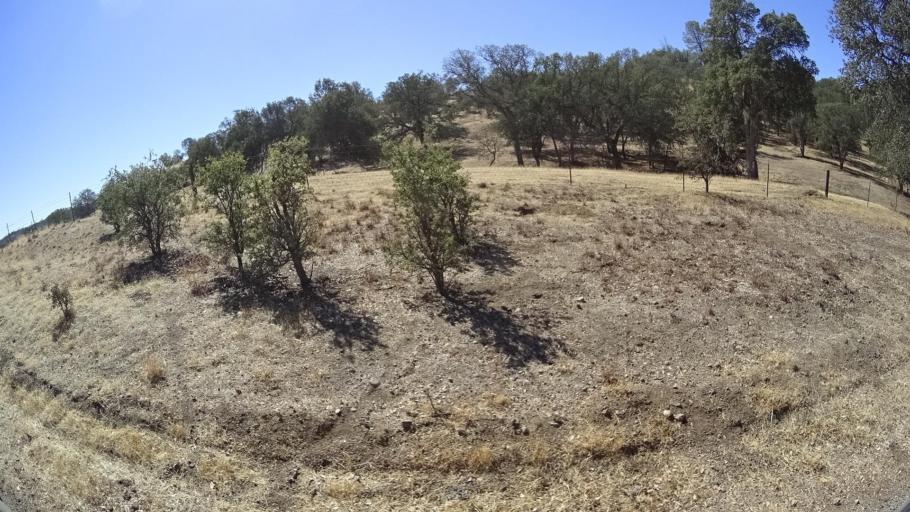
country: US
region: California
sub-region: Fresno County
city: Coalinga
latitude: 36.1836
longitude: -120.6690
